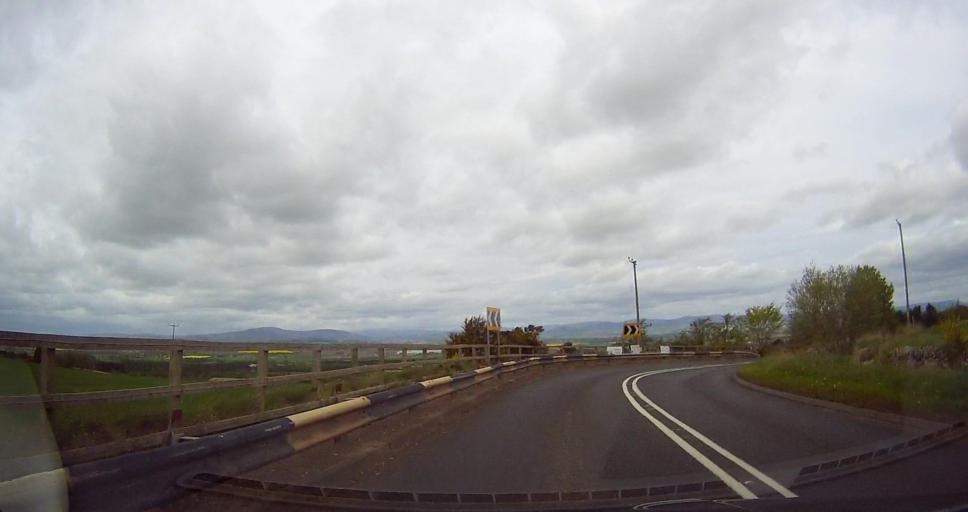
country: GB
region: Scotland
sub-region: Angus
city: Forfar
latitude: 56.6248
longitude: -2.9003
